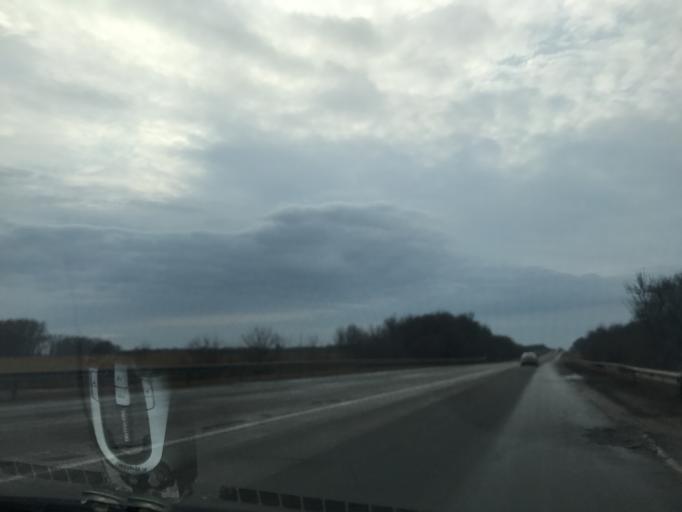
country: RU
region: Krasnodarskiy
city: Fastovetskaya
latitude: 45.9363
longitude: 40.0827
